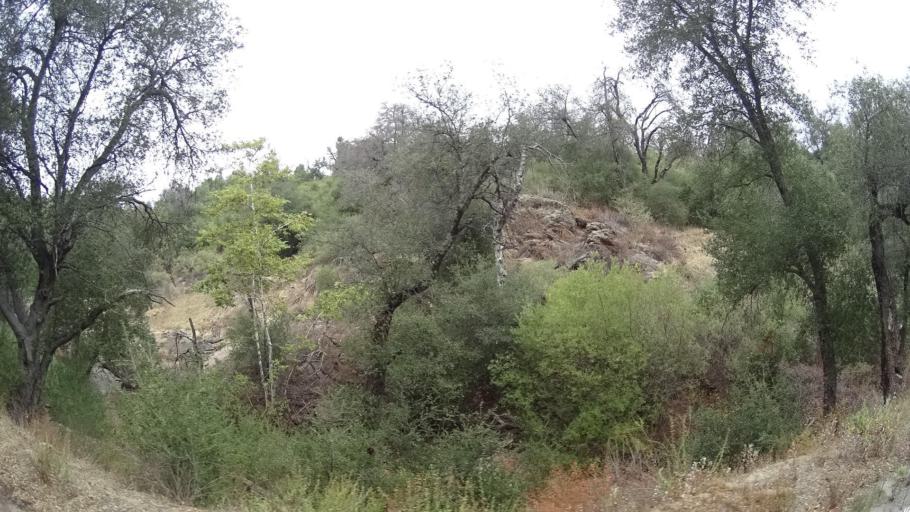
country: US
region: California
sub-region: San Diego County
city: Julian
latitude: 33.0300
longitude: -116.6367
